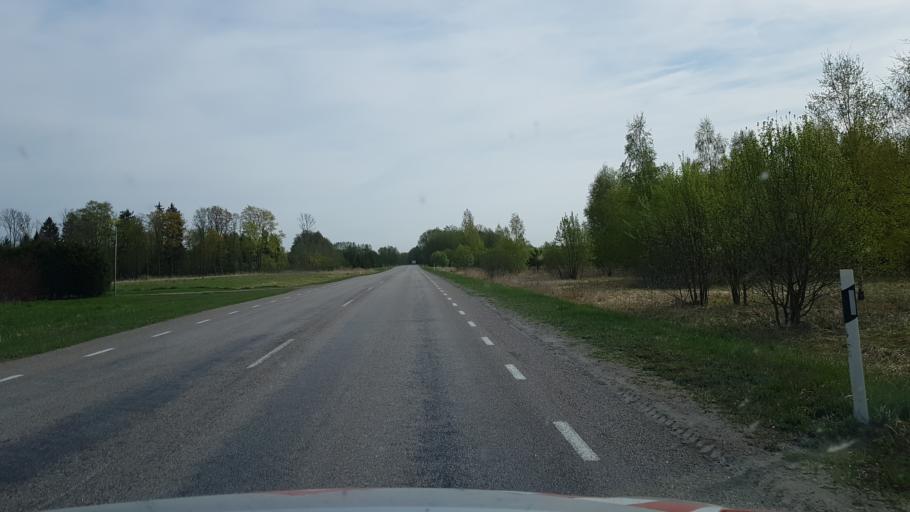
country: EE
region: Paernumaa
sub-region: Audru vald
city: Audru
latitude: 58.3967
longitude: 24.2886
